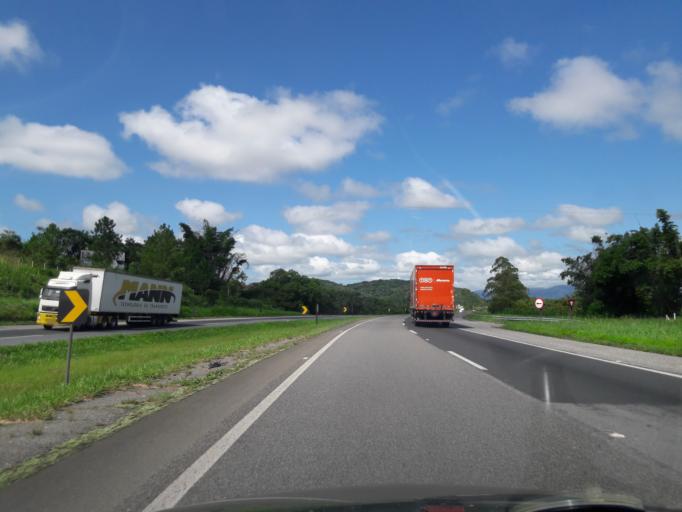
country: BR
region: Sao Paulo
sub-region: Jacupiranga
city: Jacupiranga
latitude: -24.6779
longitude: -47.9809
